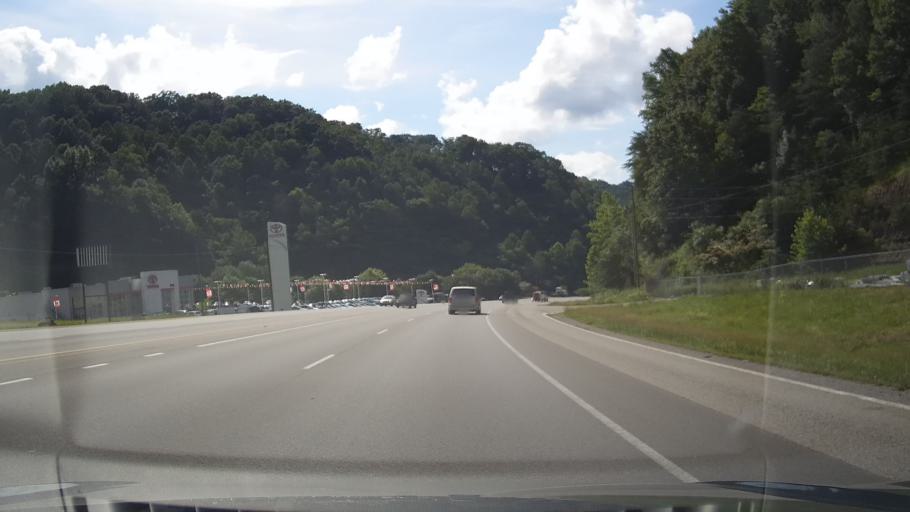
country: US
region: Kentucky
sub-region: Floyd County
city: Prestonsburg
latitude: 37.6444
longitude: -82.7751
